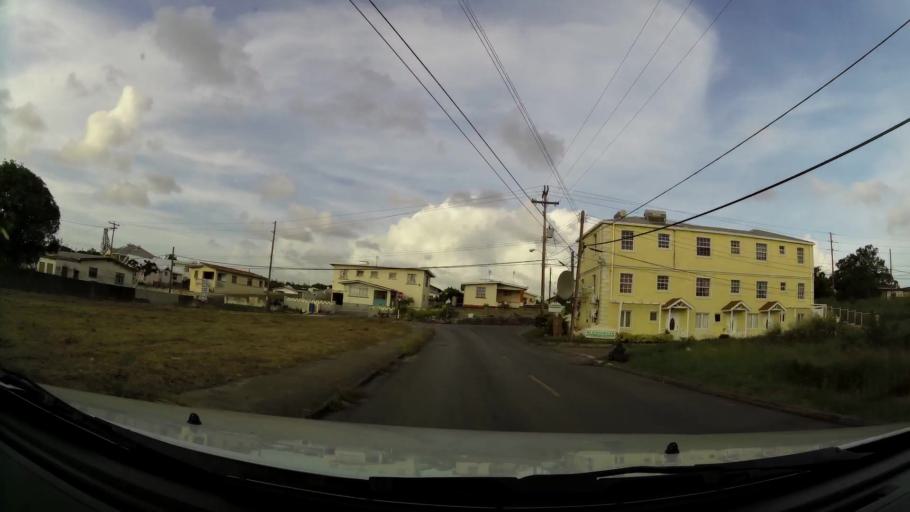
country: BB
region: Christ Church
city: Oistins
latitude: 13.0607
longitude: -59.5368
